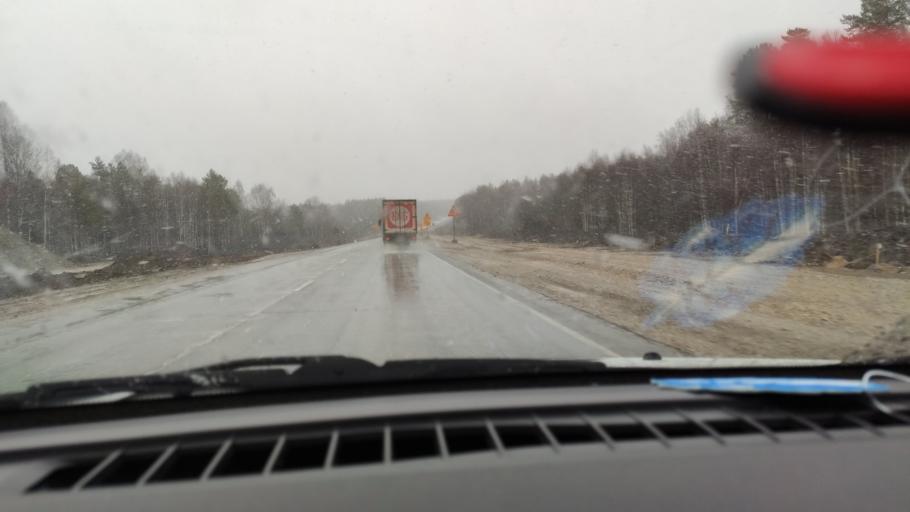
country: RU
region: Sverdlovsk
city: Bisert'
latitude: 56.8351
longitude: 58.9258
